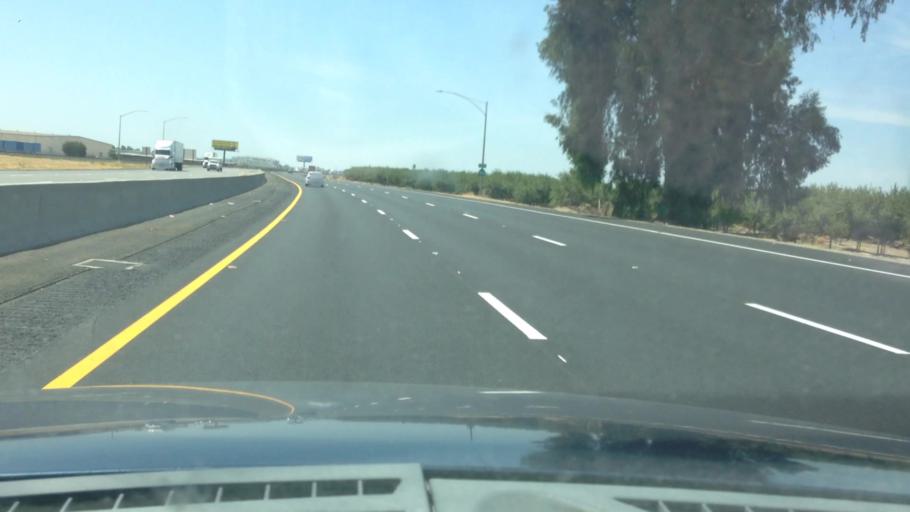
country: US
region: California
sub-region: Kern County
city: McFarland
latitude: 35.7169
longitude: -119.2370
